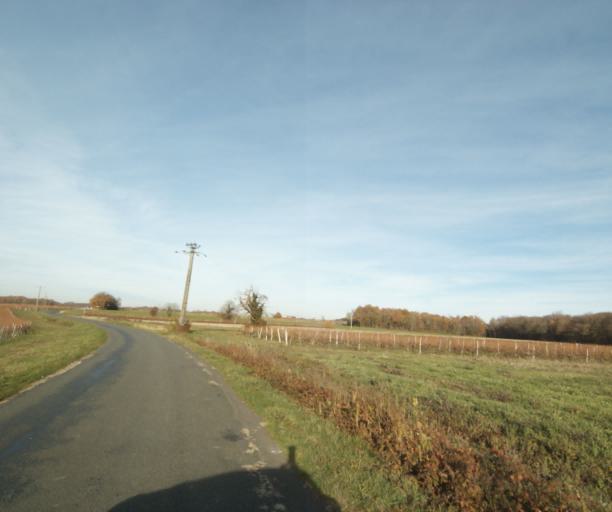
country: FR
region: Poitou-Charentes
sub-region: Departement de la Charente-Maritime
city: Chaniers
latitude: 45.7256
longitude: -0.5269
